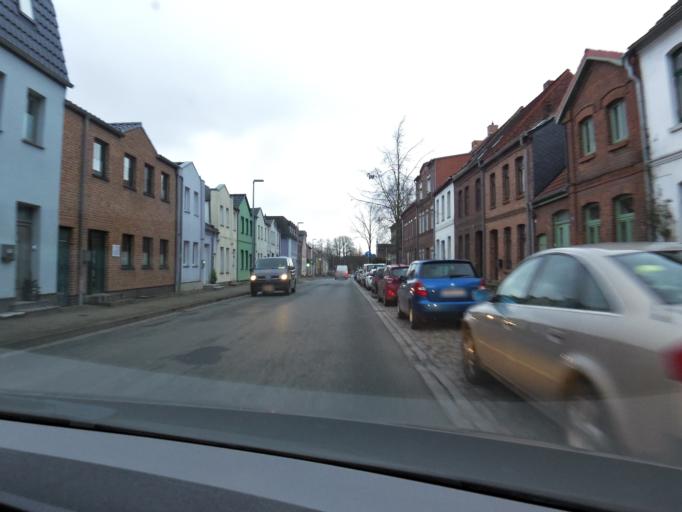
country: DE
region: Mecklenburg-Vorpommern
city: Grevesmuhlen
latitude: 53.8604
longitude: 11.1804
